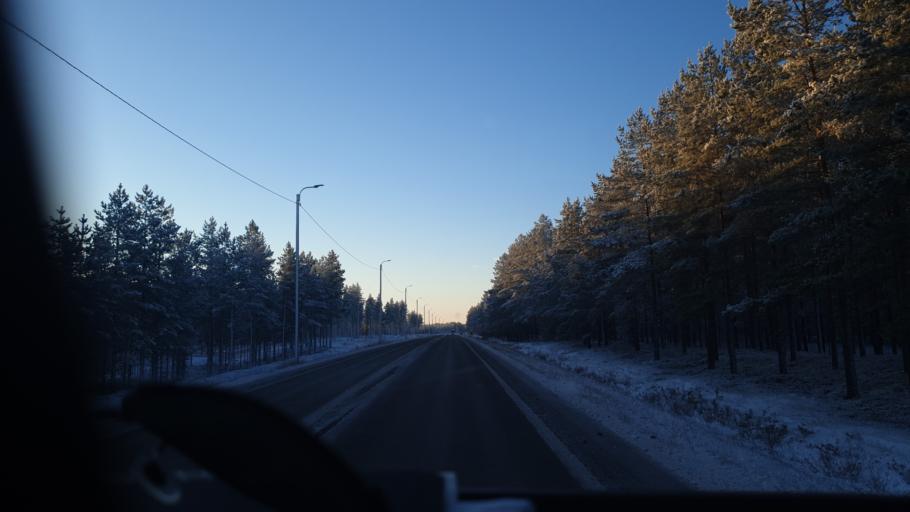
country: FI
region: Northern Ostrobothnia
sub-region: Ylivieska
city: Kalajoki
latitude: 64.2355
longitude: 23.8296
